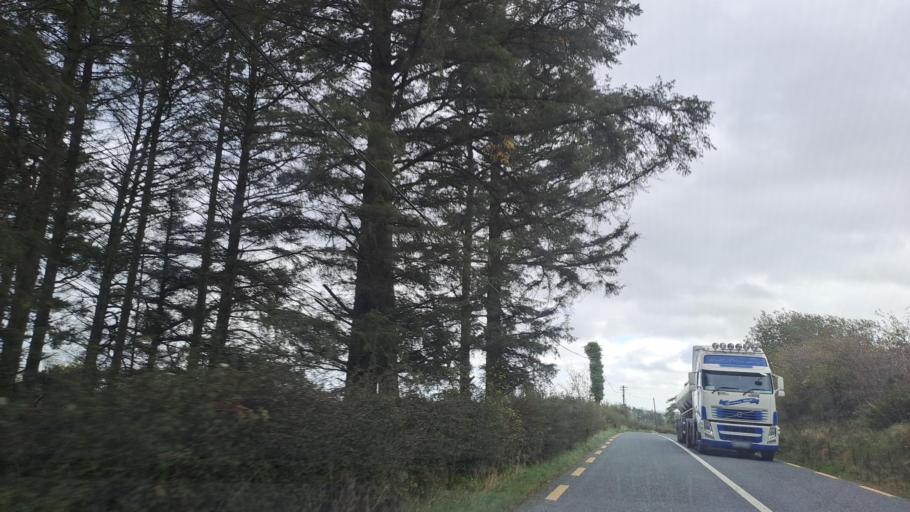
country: IE
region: Ulster
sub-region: An Cabhan
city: Kingscourt
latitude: 53.9245
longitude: -6.8715
